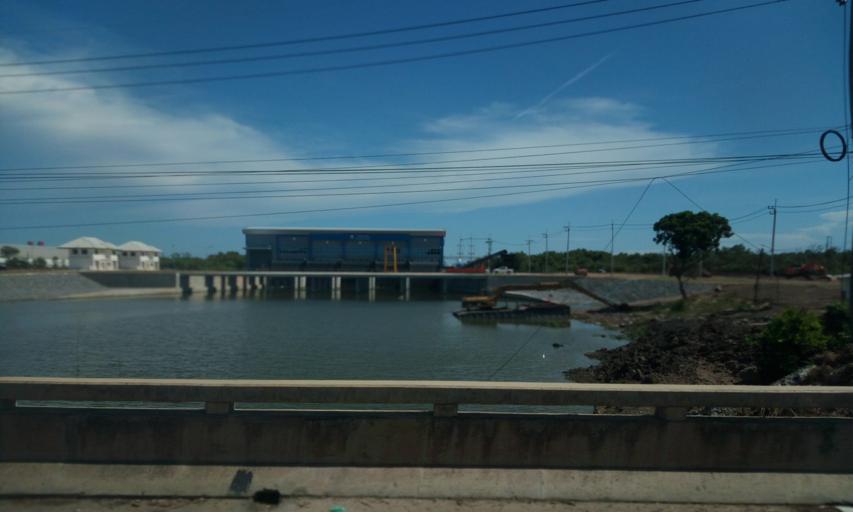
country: TH
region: Samut Prakan
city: Bang Bo District
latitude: 13.5019
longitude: 100.7642
